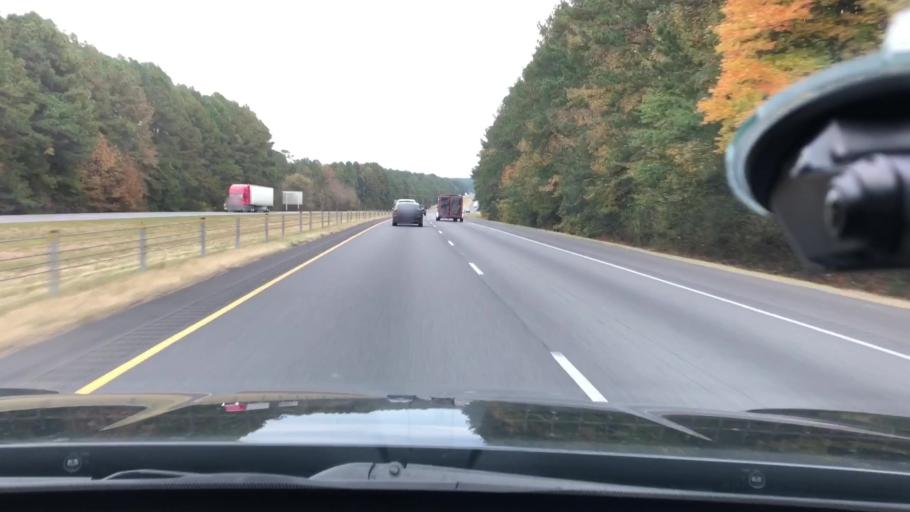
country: US
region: Arkansas
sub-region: Clark County
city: Arkadelphia
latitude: 34.2029
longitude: -93.0472
